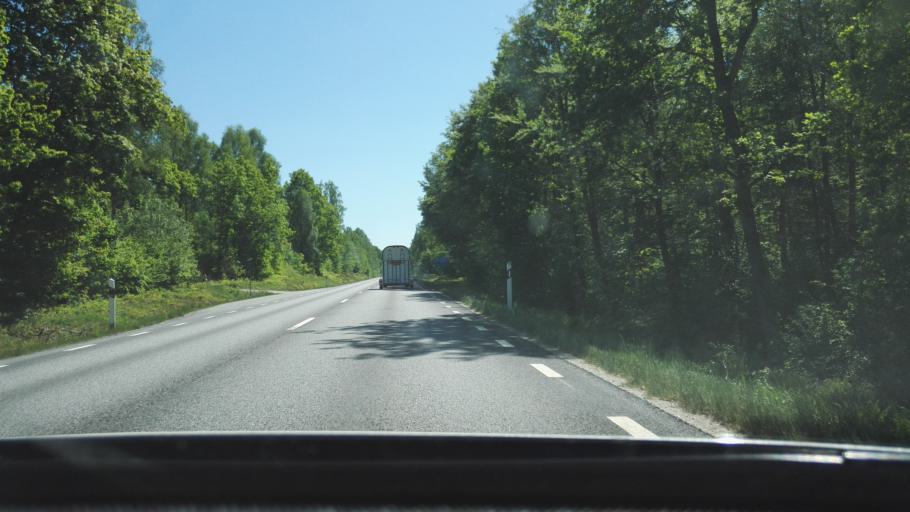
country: SE
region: Kronoberg
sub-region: Tingsryds Kommun
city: Tingsryd
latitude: 56.4866
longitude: 15.0012
